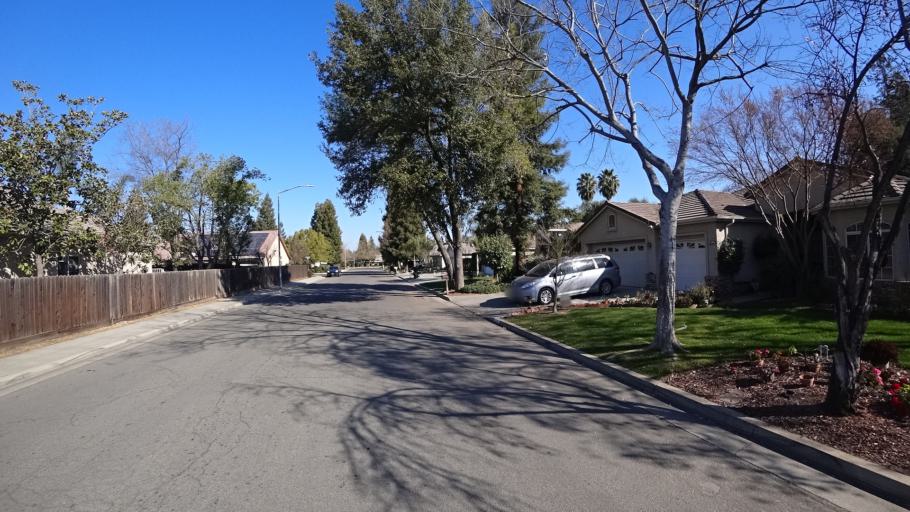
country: US
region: California
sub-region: Fresno County
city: Clovis
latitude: 36.8762
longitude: -119.7518
